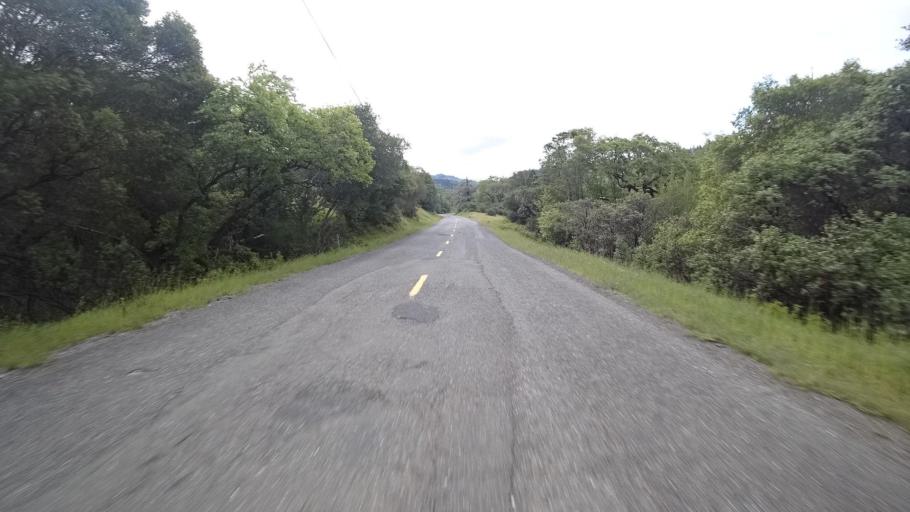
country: US
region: California
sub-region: Humboldt County
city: Redway
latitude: 40.2001
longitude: -123.5937
